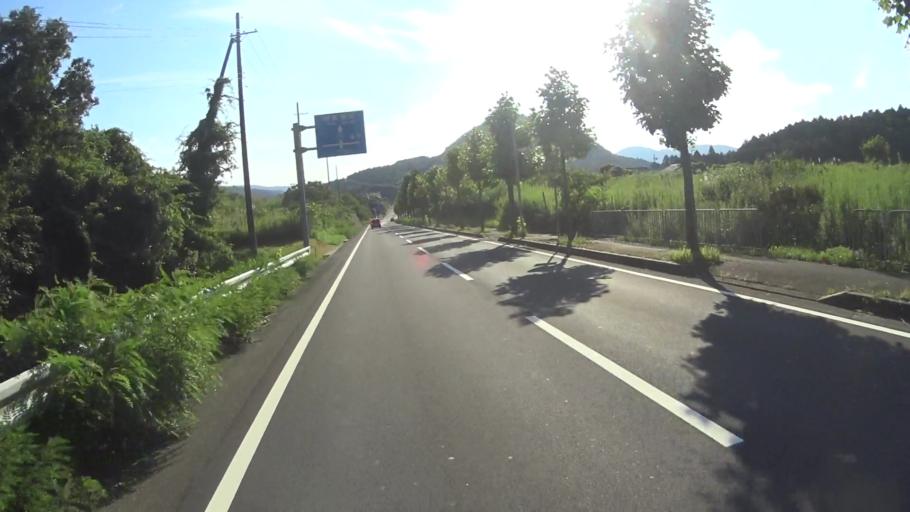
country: JP
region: Hyogo
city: Toyooka
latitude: 35.6188
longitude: 134.9245
